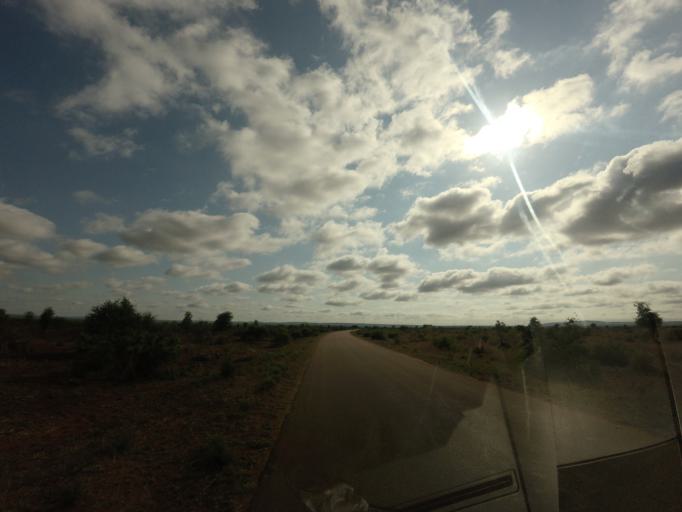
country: ZA
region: Mpumalanga
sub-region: Ehlanzeni District
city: Komatipoort
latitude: -25.1791
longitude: 31.9055
